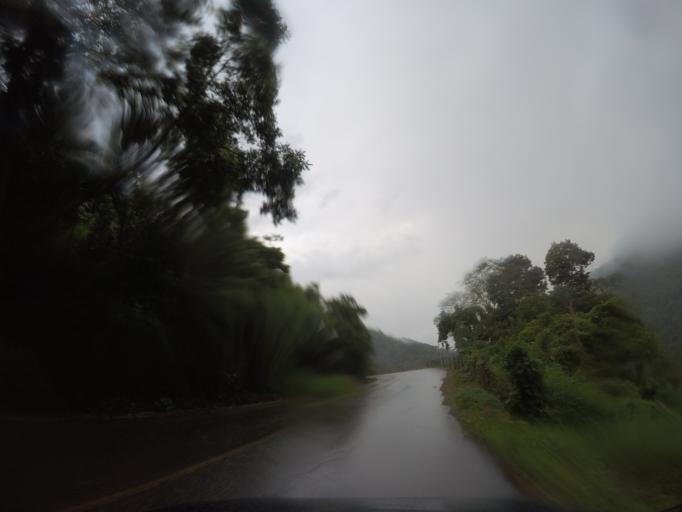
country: MX
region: Oaxaca
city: San Gabriel Mixtepec
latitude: 16.0708
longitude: -97.0776
